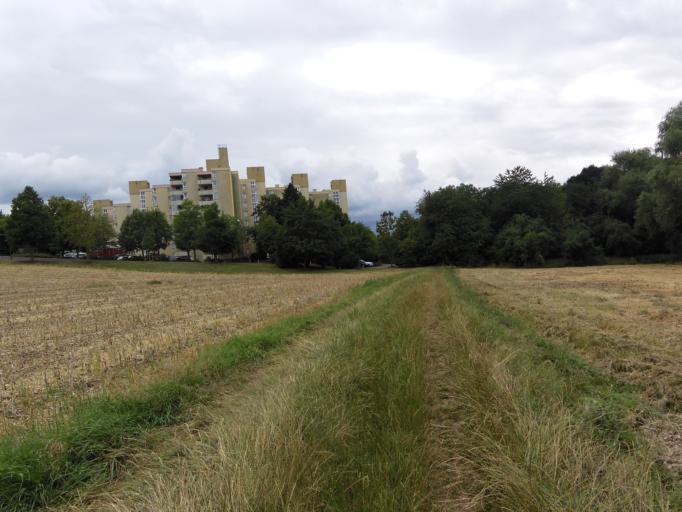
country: DE
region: Bavaria
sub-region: Regierungsbezirk Unterfranken
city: Wuerzburg
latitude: 49.8148
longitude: 9.9756
